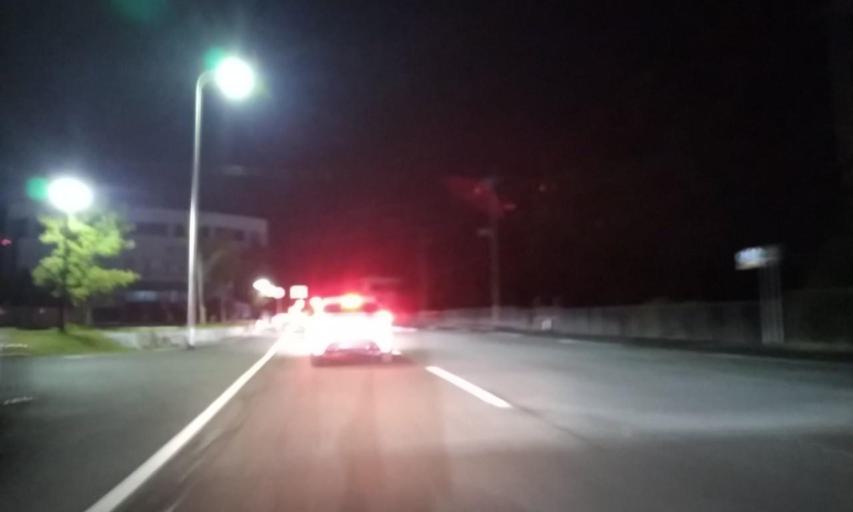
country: JP
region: Kyoto
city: Maizuru
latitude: 35.4784
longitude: 135.3892
